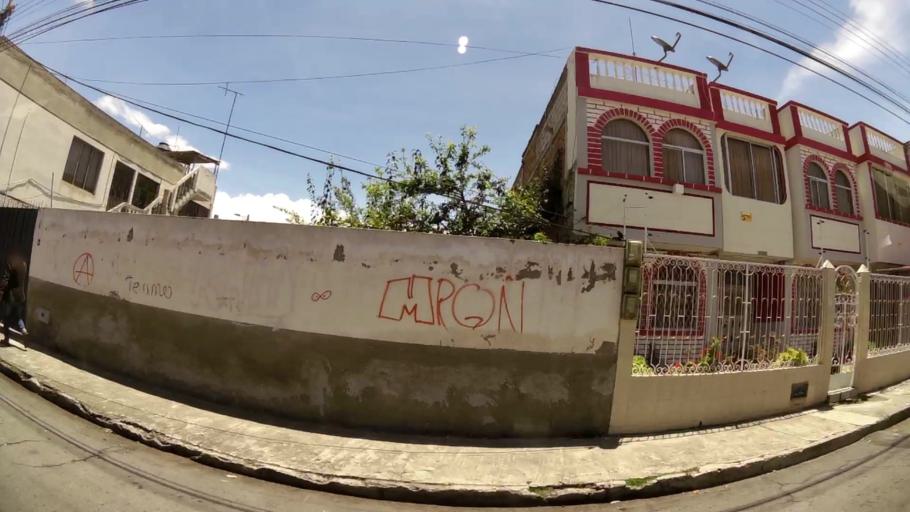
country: EC
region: Chimborazo
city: Riobamba
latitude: -1.6794
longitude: -78.6552
